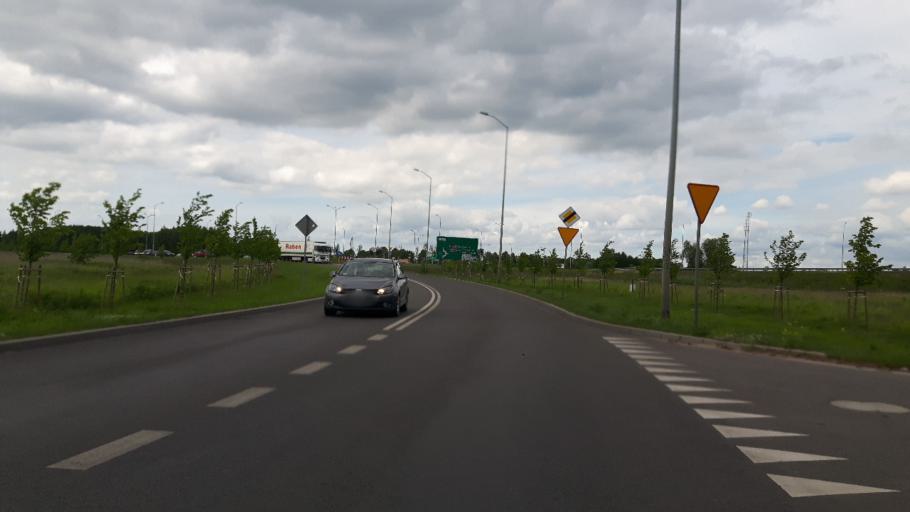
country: PL
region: West Pomeranian Voivodeship
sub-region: Szczecin
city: Szczecin
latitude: 53.4077
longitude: 14.6981
